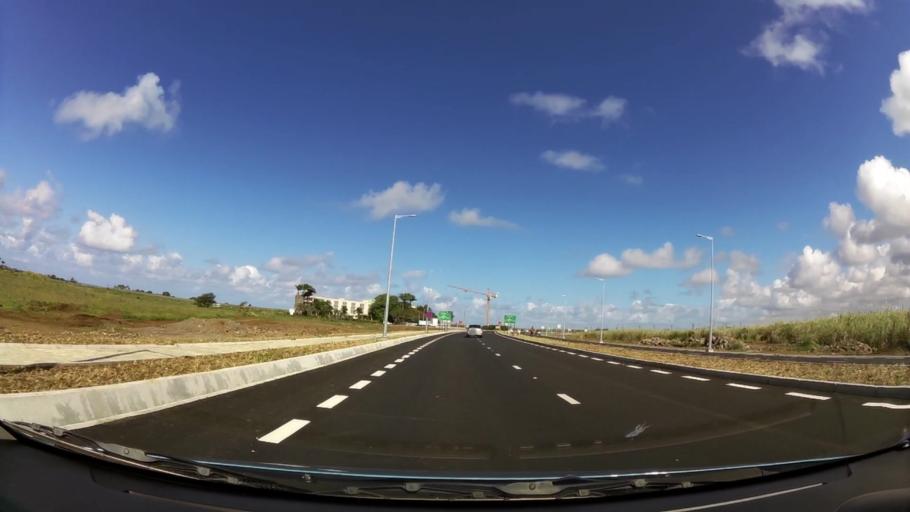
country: MU
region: Grand Port
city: Plaine Magnien
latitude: -20.4374
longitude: 57.6724
